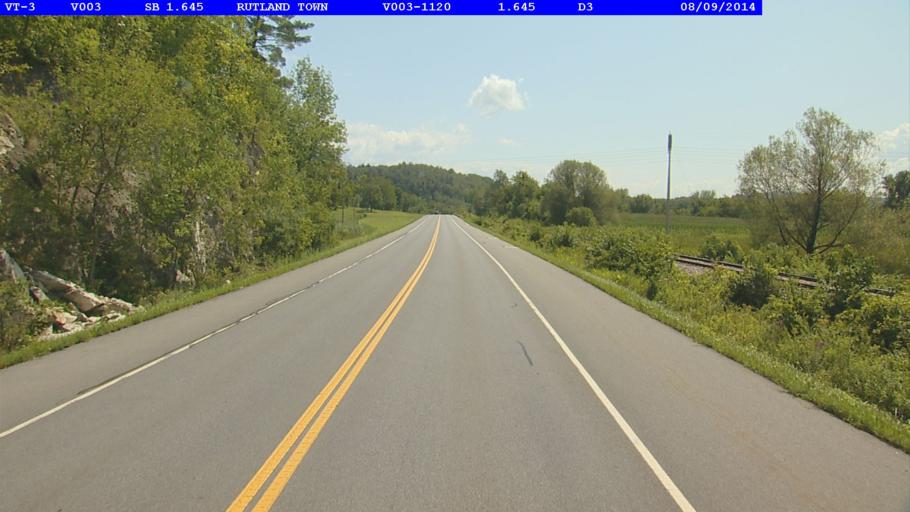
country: US
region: Vermont
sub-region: Rutland County
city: West Rutland
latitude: 43.6248
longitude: -73.0278
